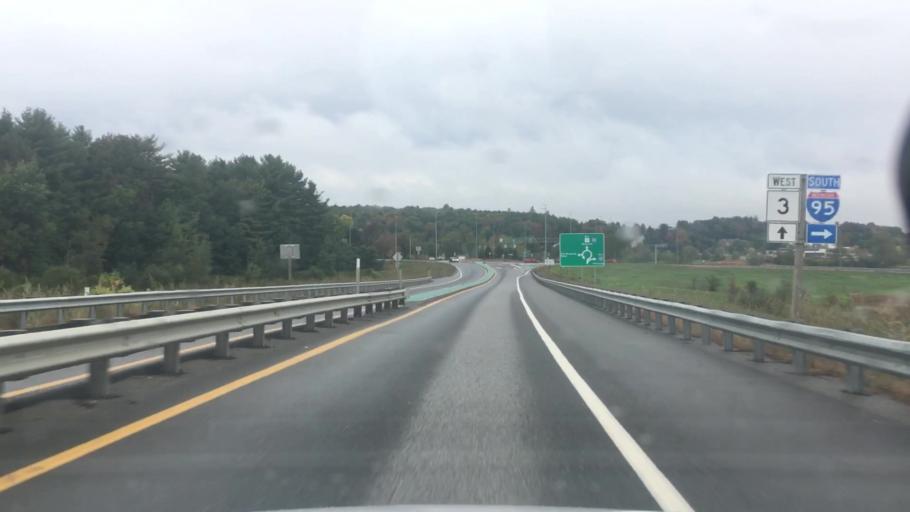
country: US
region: Maine
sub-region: Kennebec County
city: Augusta
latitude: 44.3557
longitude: -69.7829
